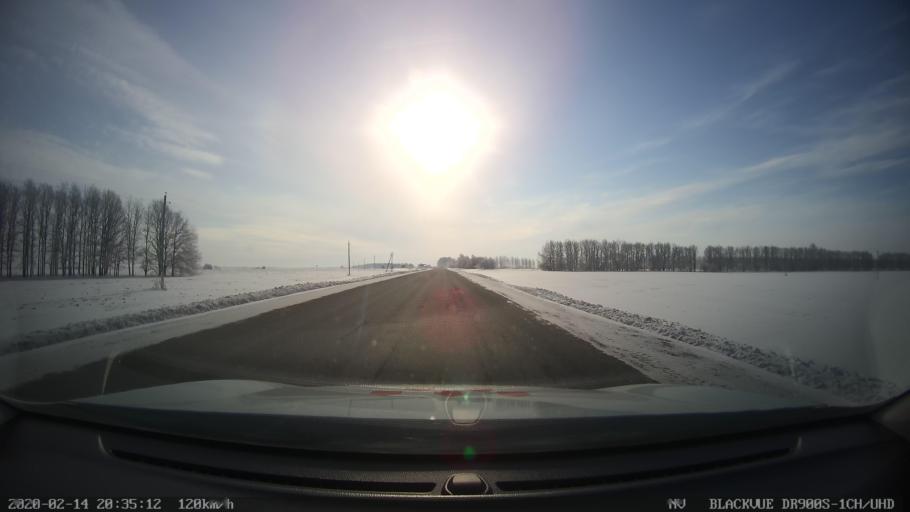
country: RU
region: Tatarstan
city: Kuybyshevskiy Zaton
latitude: 55.3858
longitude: 48.9808
